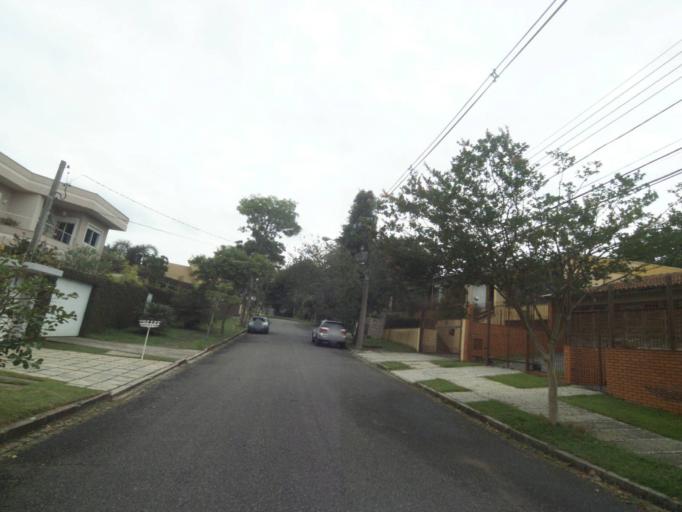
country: BR
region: Parana
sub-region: Curitiba
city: Curitiba
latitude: -25.4037
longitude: -49.2839
